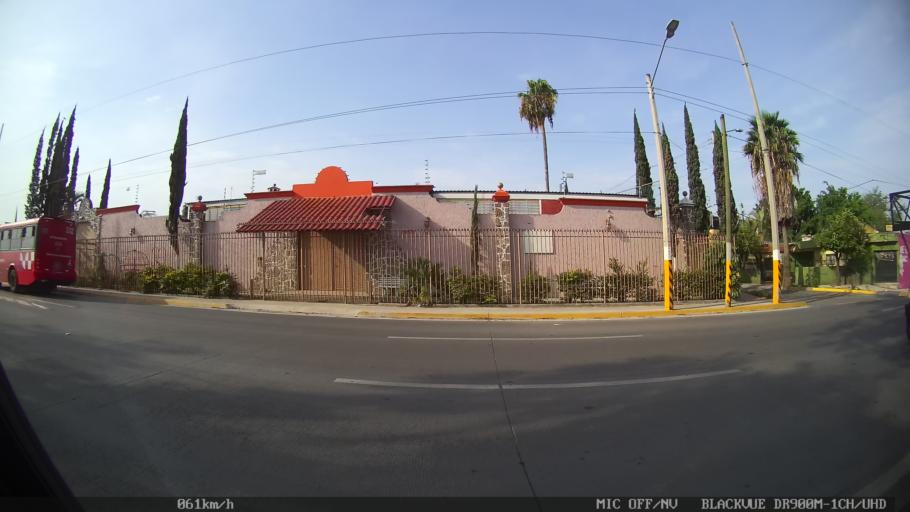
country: MX
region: Jalisco
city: Tlaquepaque
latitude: 20.7123
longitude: -103.2932
